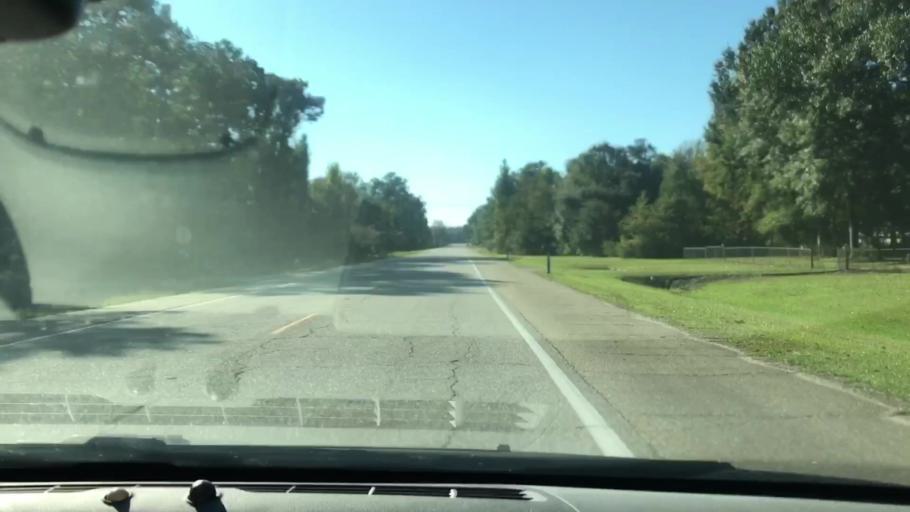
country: US
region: Mississippi
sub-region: Pearl River County
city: Nicholson
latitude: 30.4889
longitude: -89.8104
